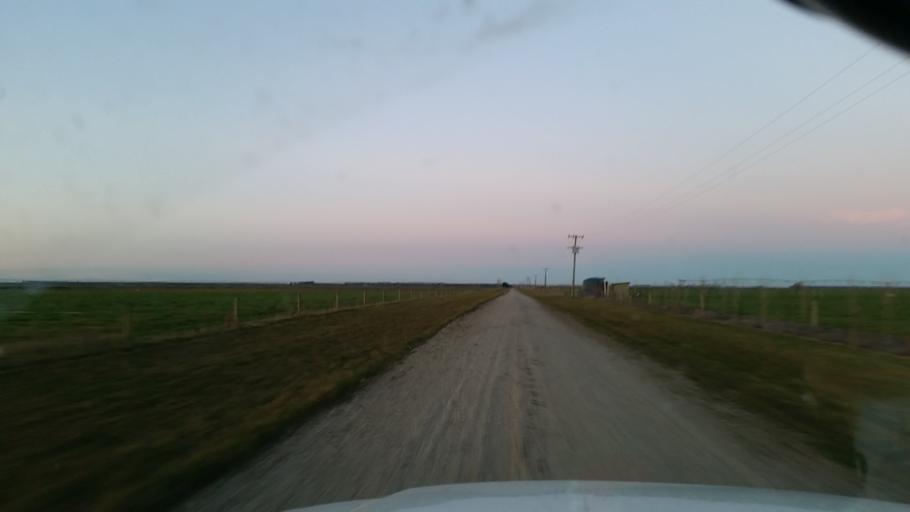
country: NZ
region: Canterbury
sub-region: Ashburton District
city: Tinwald
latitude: -43.9398
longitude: 171.5514
